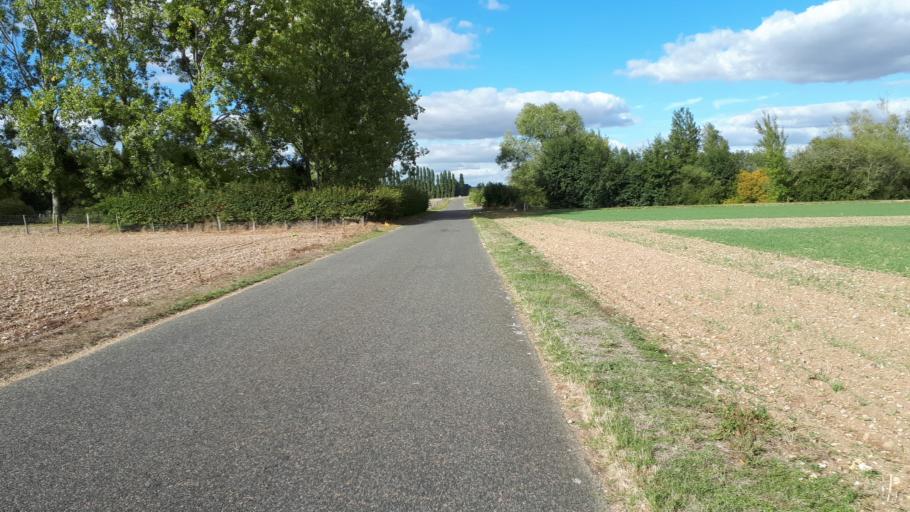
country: FR
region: Centre
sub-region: Departement du Loir-et-Cher
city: Villiers-sur-Loir
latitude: 47.7952
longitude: 0.9567
